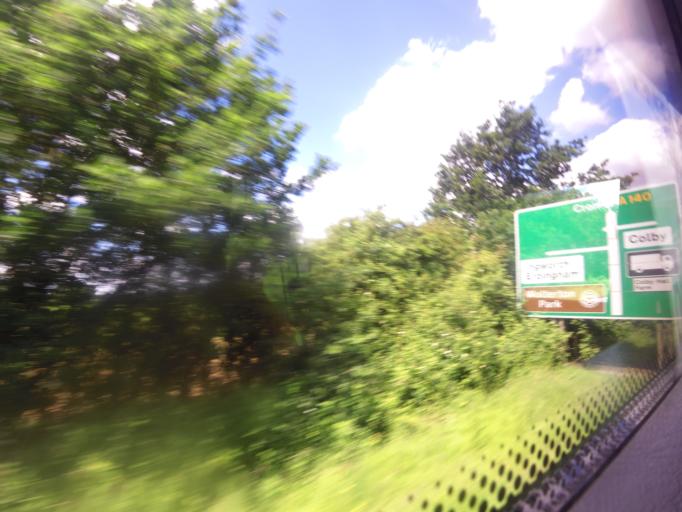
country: GB
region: England
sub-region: Norfolk
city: Aylsham
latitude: 52.8324
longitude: 1.2720
